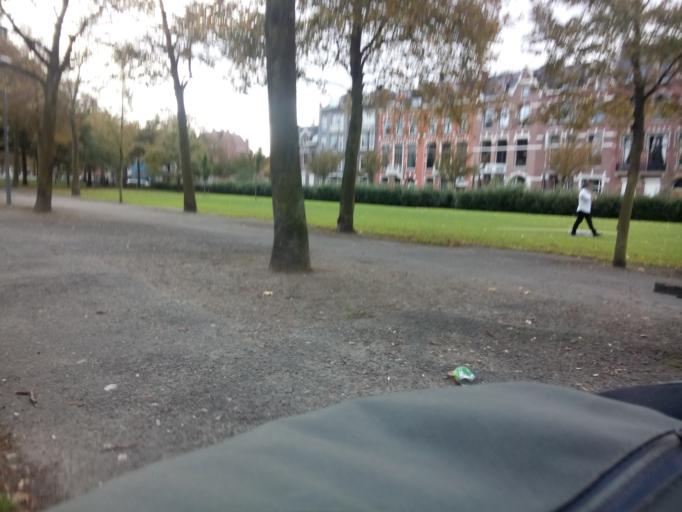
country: NL
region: South Holland
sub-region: Gemeente Rotterdam
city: Delfshaven
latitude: 51.9156
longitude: 4.4550
